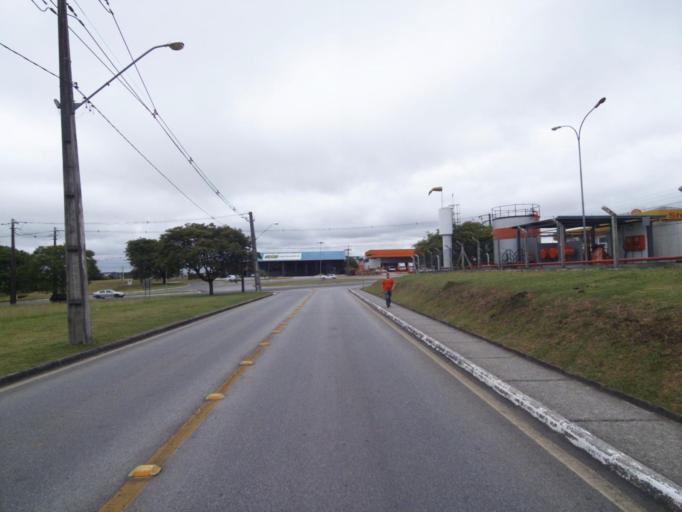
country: BR
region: Parana
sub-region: Sao Jose Dos Pinhais
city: Sao Jose dos Pinhais
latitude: -25.5334
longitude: -49.1772
